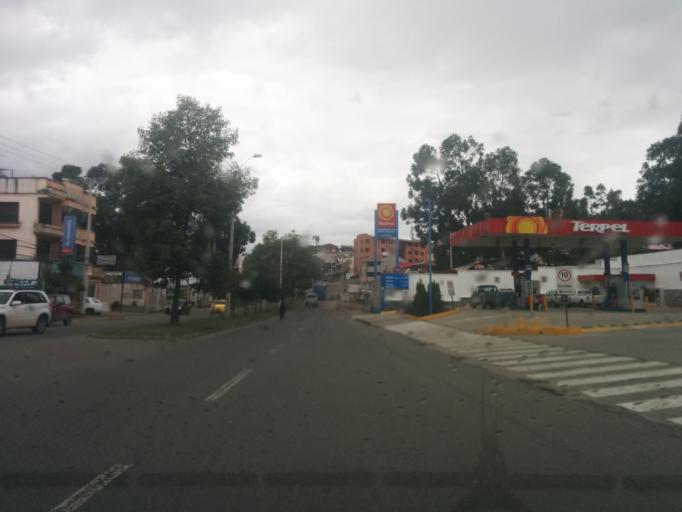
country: EC
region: Azuay
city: Cuenca
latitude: -2.8901
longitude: -78.9655
